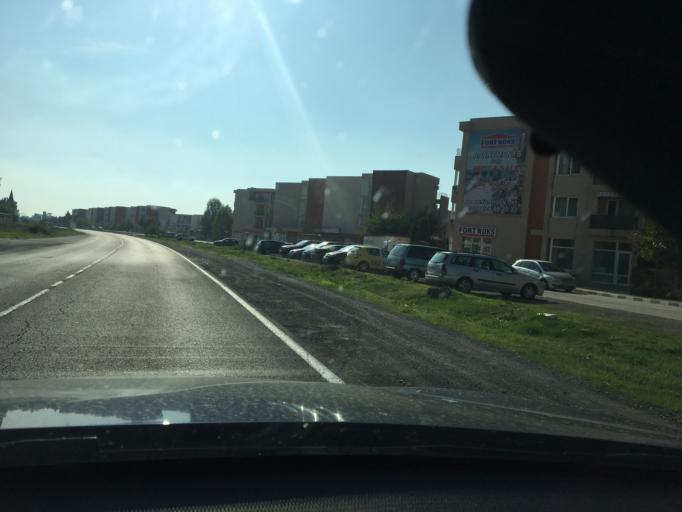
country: BG
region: Burgas
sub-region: Obshtina Nesebur
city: Nesebar
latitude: 42.7032
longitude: 27.7063
